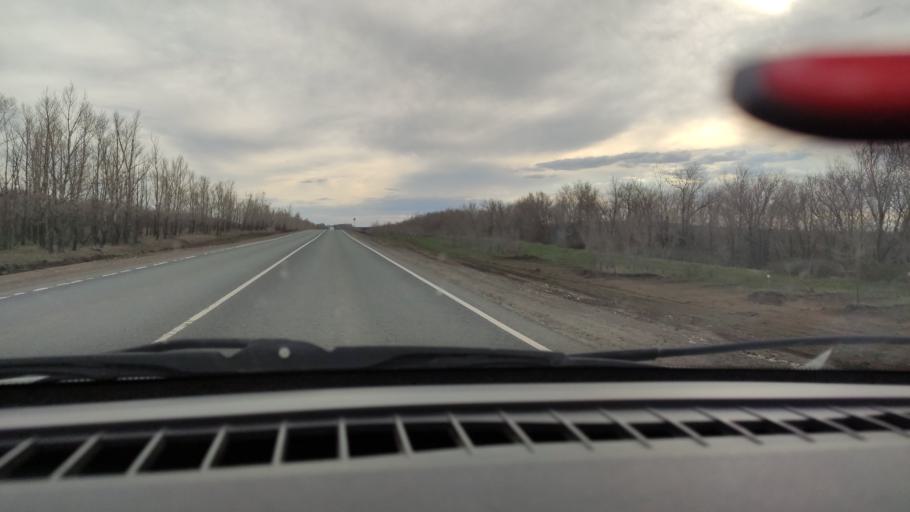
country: RU
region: Orenburg
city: Sakmara
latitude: 52.3180
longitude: 55.4725
